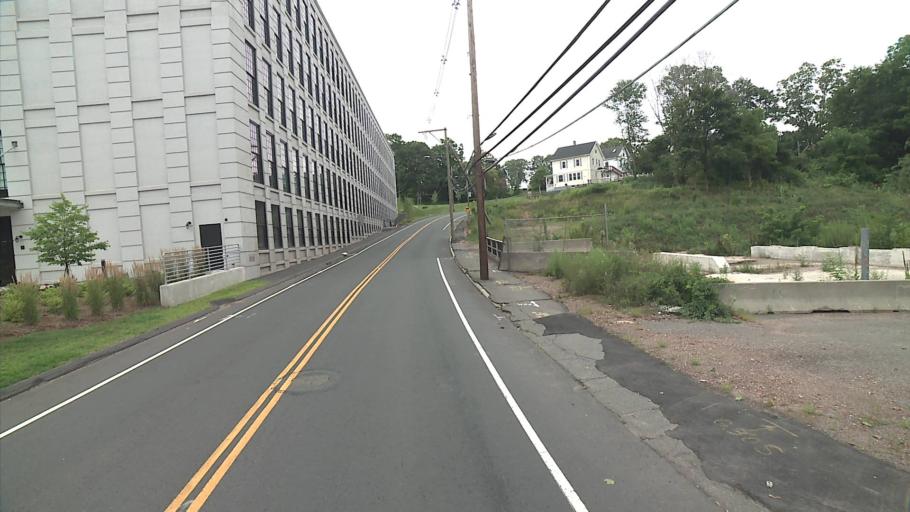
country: US
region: Connecticut
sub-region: Tolland County
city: Rockville
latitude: 41.8680
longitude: -72.4337
